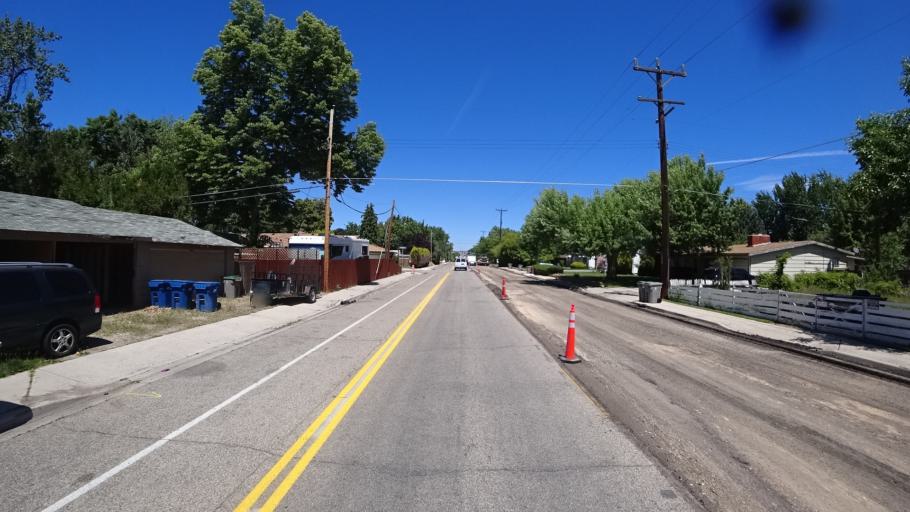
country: US
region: Idaho
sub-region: Ada County
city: Garden City
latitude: 43.5915
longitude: -116.2287
